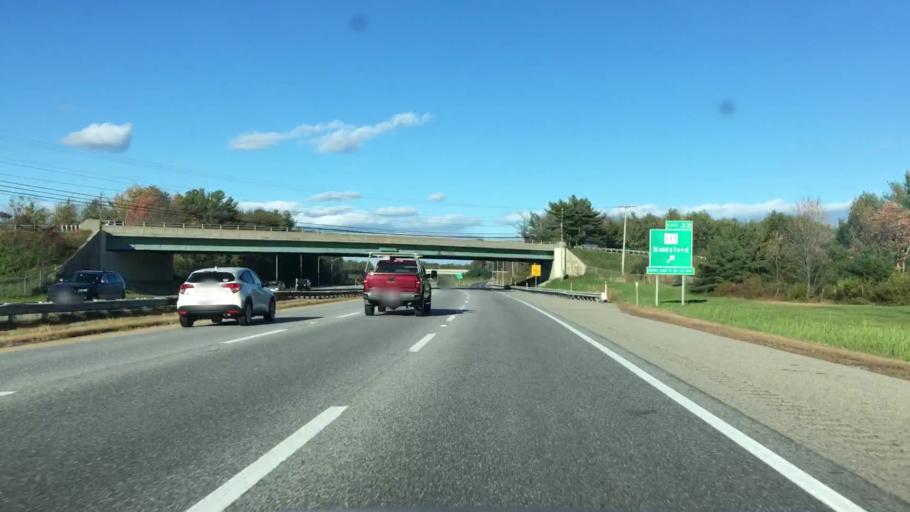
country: US
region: Maine
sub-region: York County
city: Biddeford
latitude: 43.4761
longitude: -70.5035
